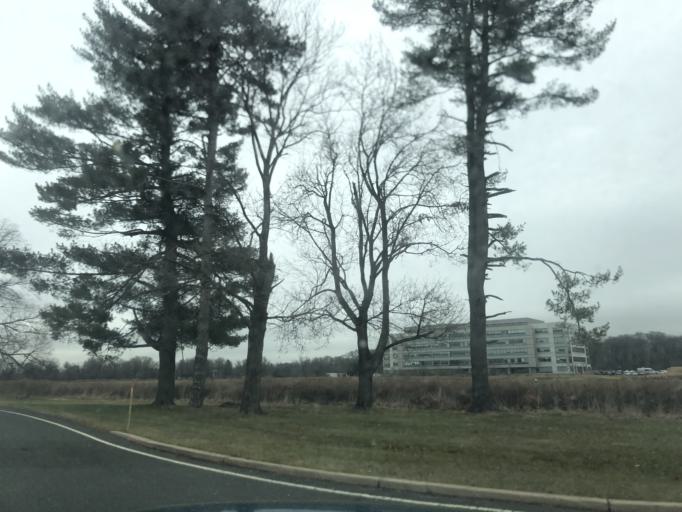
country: US
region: New Jersey
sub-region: Somerset County
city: Kingston
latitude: 40.3500
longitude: -74.6138
